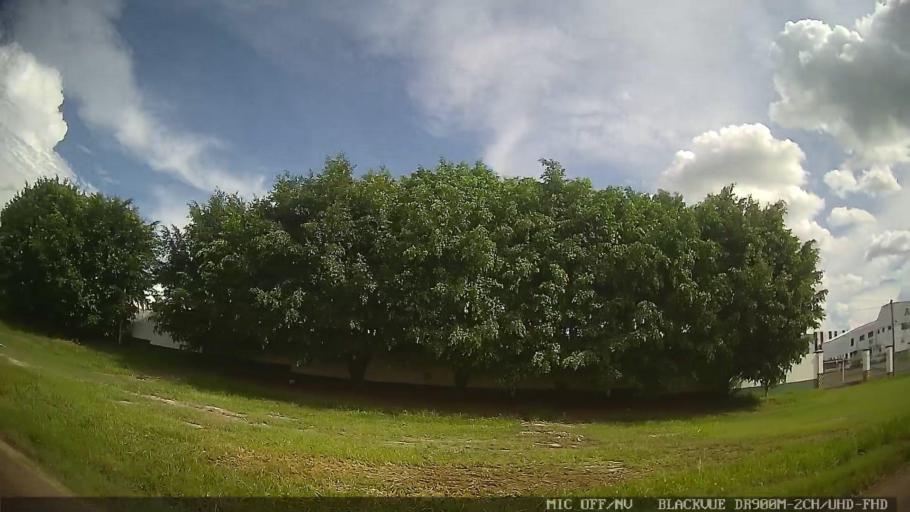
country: BR
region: Sao Paulo
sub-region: Laranjal Paulista
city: Laranjal Paulista
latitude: -23.0414
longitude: -47.9049
